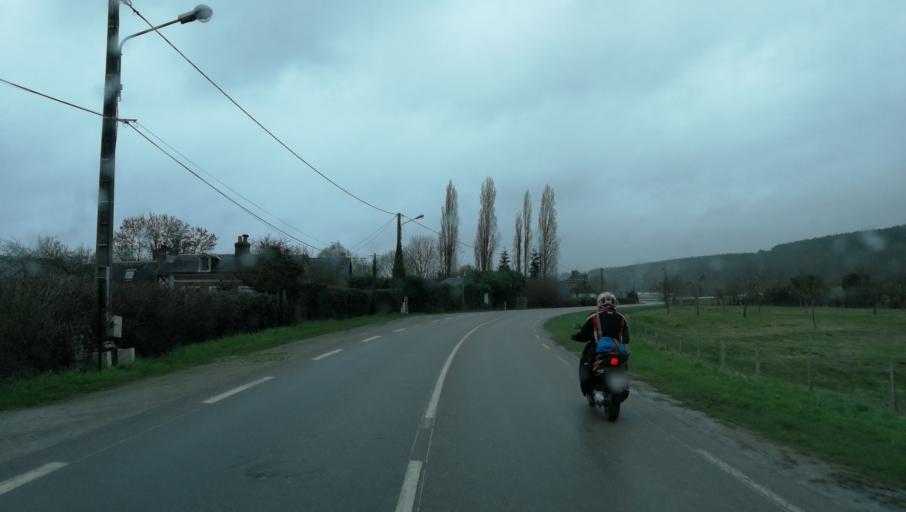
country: FR
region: Haute-Normandie
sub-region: Departement de l'Eure
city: Brionne
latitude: 49.1706
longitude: 0.7233
